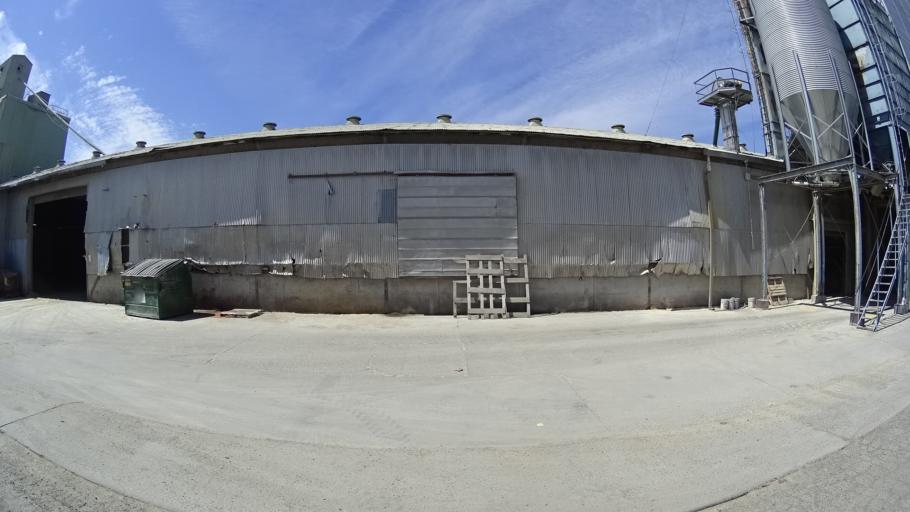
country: US
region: California
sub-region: Glenn County
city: Willows
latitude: 39.6231
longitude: -122.1932
